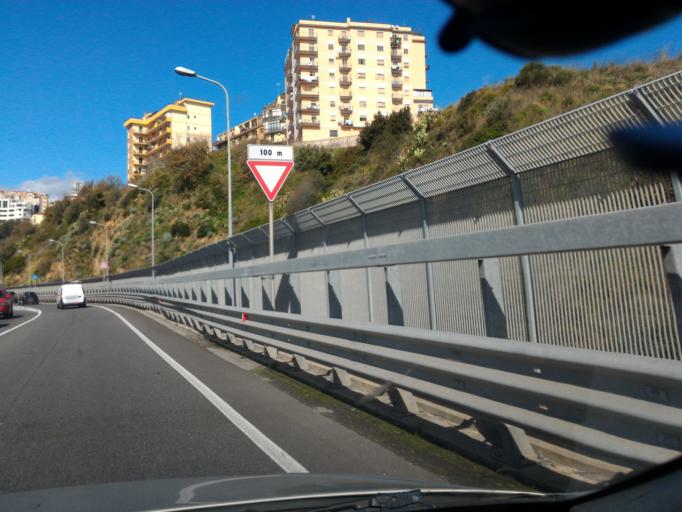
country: IT
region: Calabria
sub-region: Provincia di Catanzaro
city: Siano
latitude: 38.9119
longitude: 16.5937
